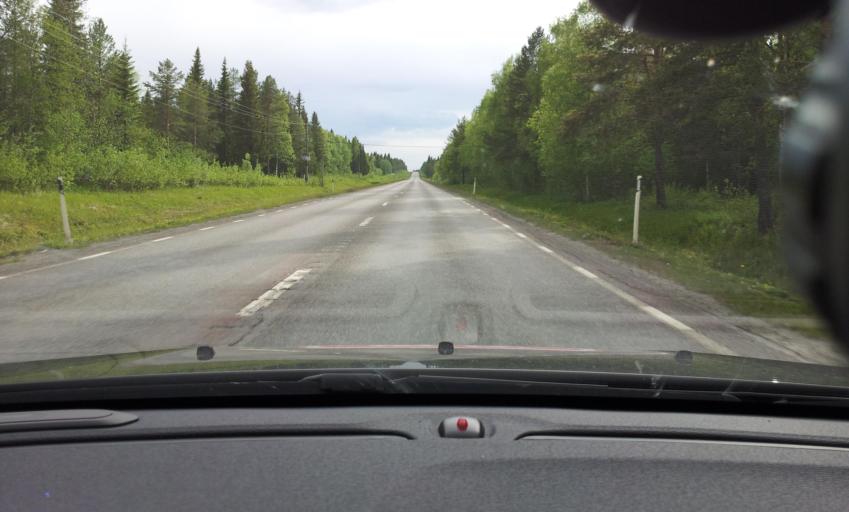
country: SE
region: Jaemtland
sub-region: OEstersunds Kommun
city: Lit
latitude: 63.2006
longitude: 14.7937
